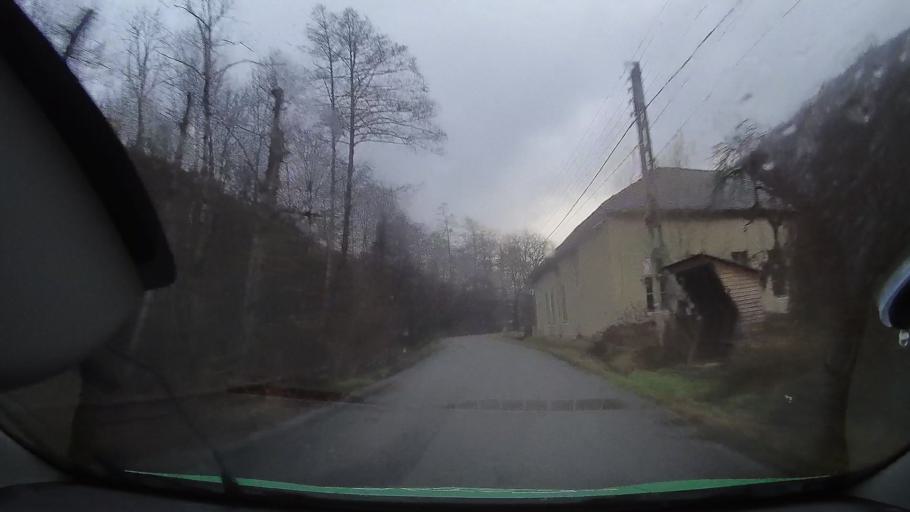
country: RO
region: Hunedoara
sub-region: Comuna Ribita
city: Ribita
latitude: 46.2616
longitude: 22.7435
